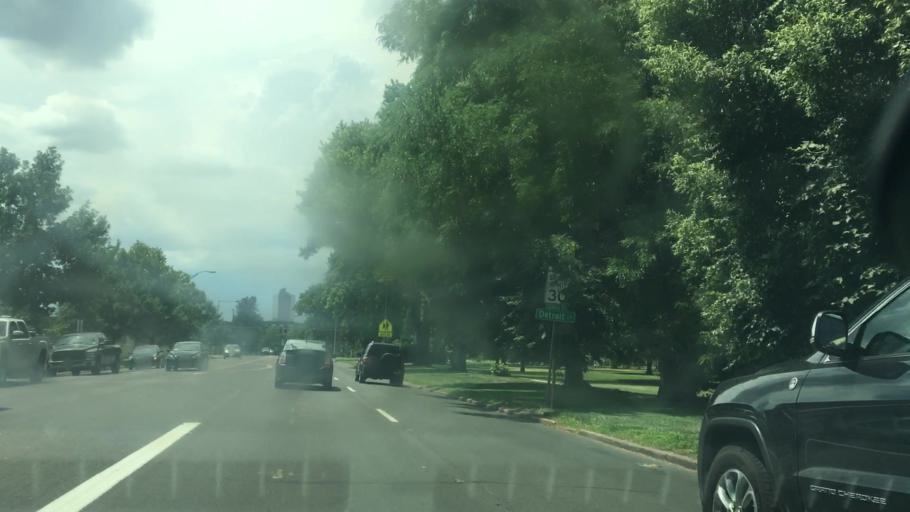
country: US
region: Colorado
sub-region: Denver County
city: Denver
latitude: 39.7439
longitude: -104.9546
